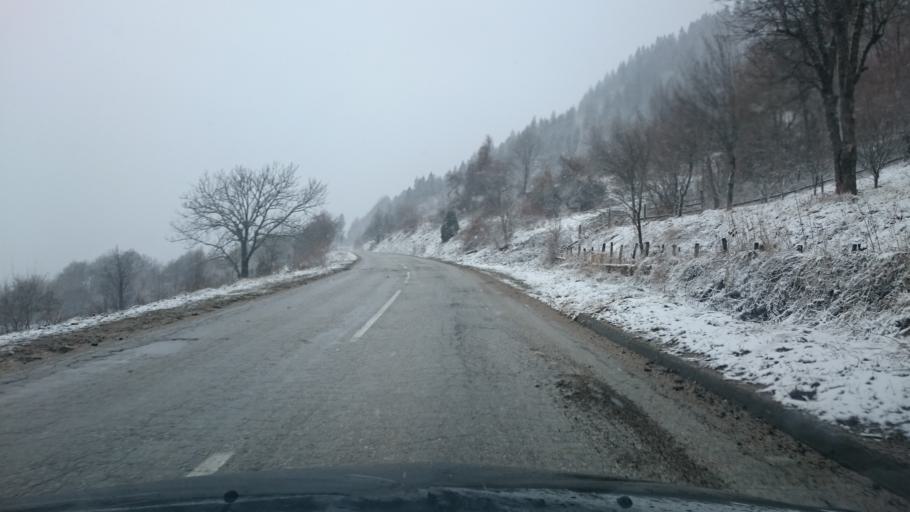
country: BA
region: Federation of Bosnia and Herzegovina
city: Turbe
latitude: 44.2700
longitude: 17.5215
